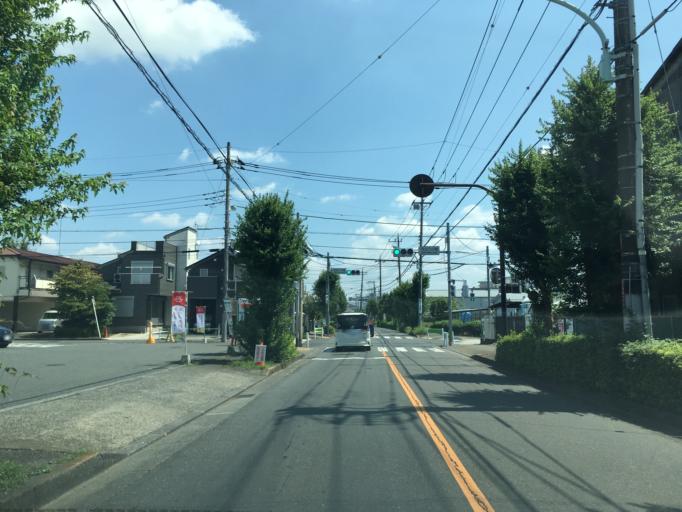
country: JP
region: Tokyo
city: Fussa
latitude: 35.7478
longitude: 139.3773
